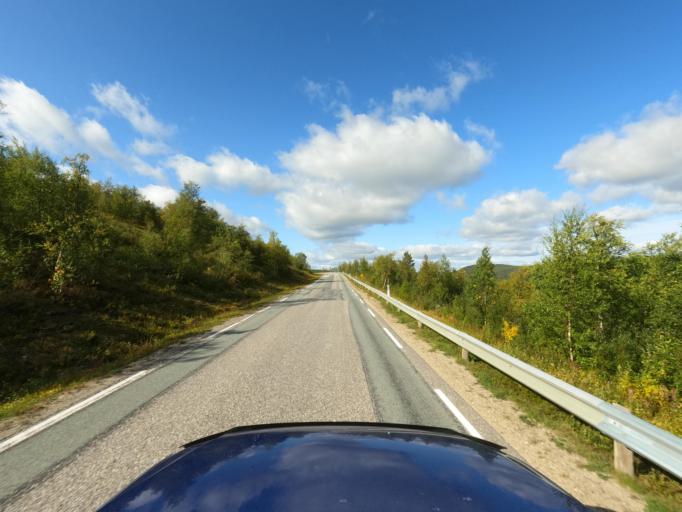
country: NO
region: Finnmark Fylke
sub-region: Karasjok
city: Karasjohka
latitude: 69.4370
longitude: 25.6657
